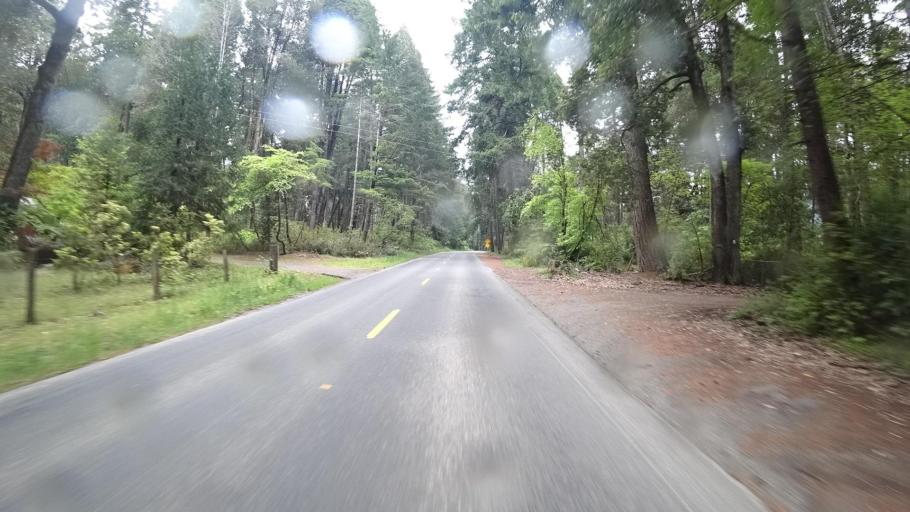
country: US
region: California
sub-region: Humboldt County
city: Willow Creek
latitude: 41.0552
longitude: -123.6721
